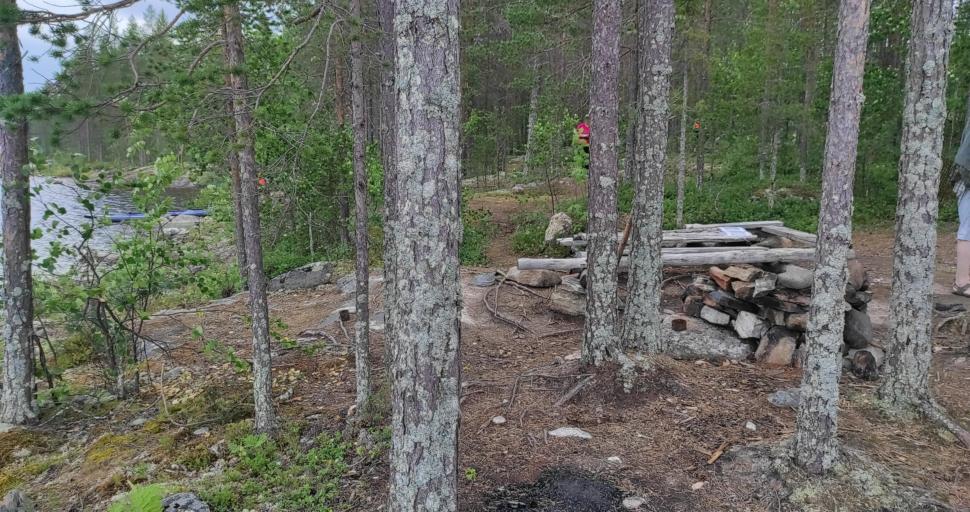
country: RU
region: Murmansk
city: Zelenoborskiy
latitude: 66.8008
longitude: 32.2093
